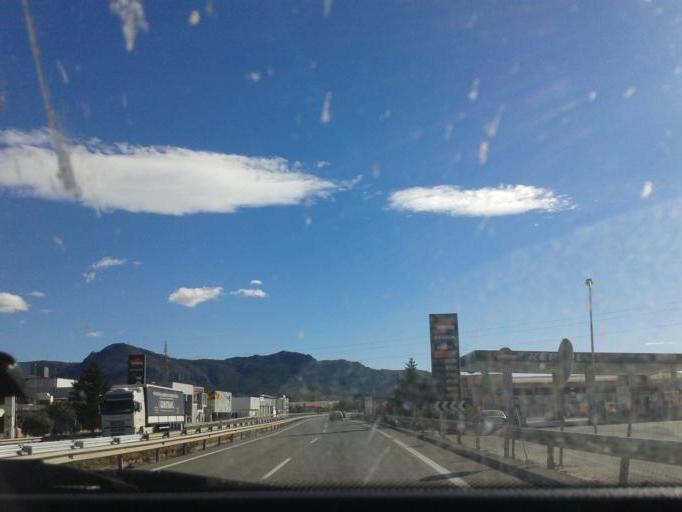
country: ES
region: Valencia
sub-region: Provincia de Alicante
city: Villena
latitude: 38.6189
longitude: -0.8492
